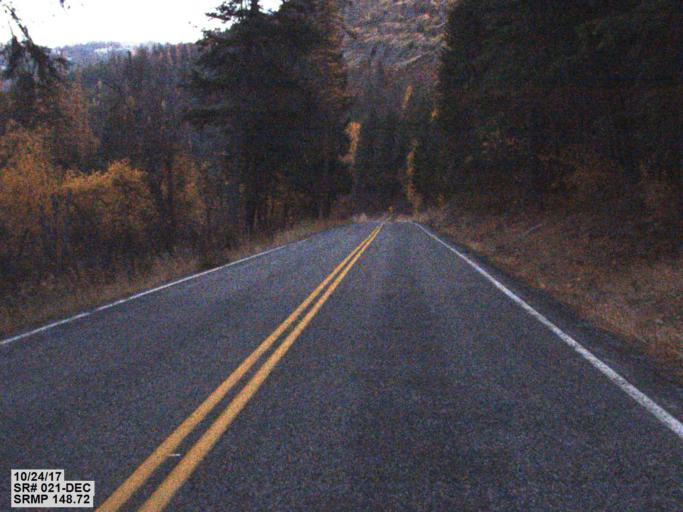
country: US
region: Washington
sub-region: Ferry County
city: Republic
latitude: 48.4871
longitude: -118.7388
